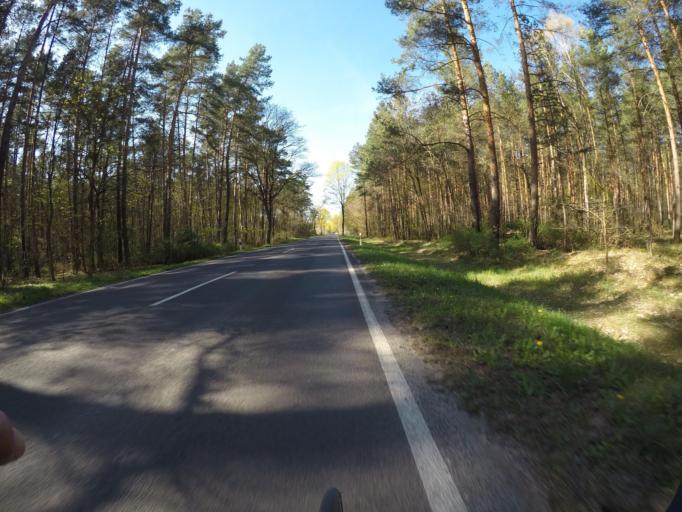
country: DE
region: Brandenburg
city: Grunheide
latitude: 52.4566
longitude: 13.8650
